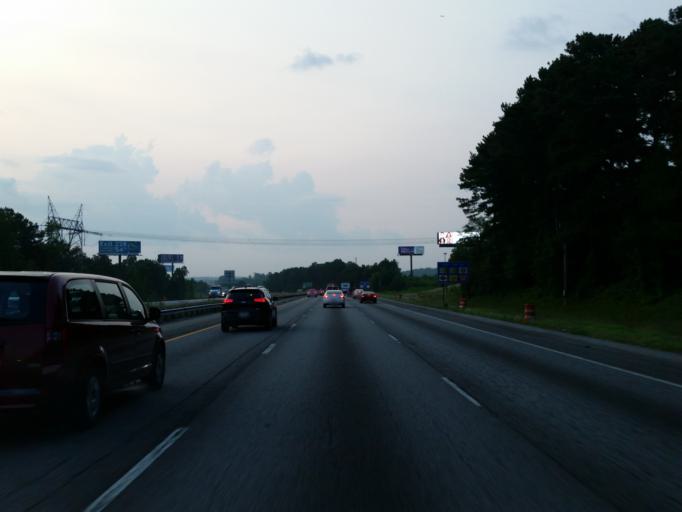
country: US
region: Georgia
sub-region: Henry County
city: Stockbridge
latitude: 33.4899
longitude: -84.2192
